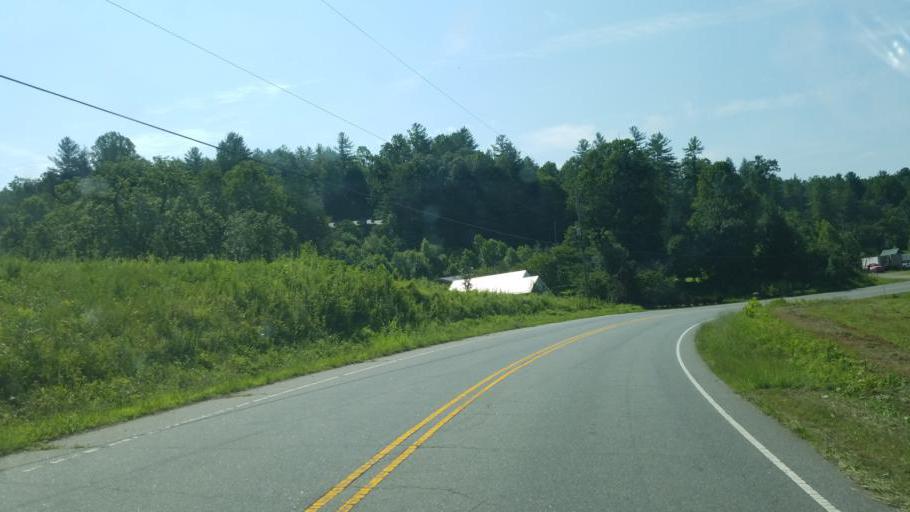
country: US
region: North Carolina
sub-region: Burke County
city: Glen Alpine
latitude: 35.8485
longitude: -81.7723
